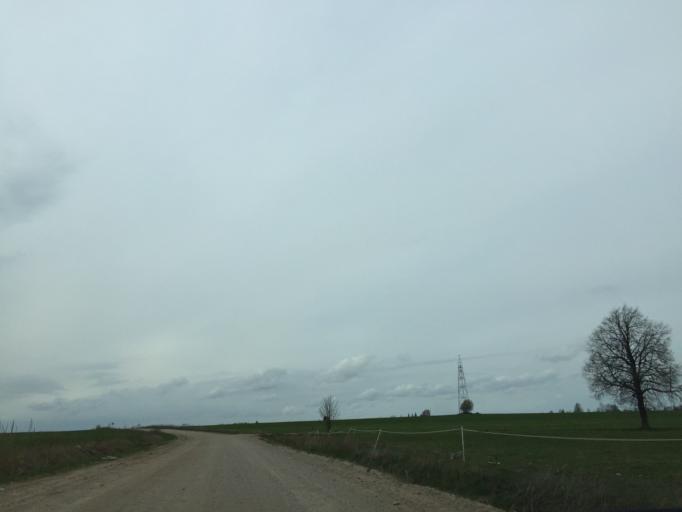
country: LV
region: Priekuli
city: Priekuli
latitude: 57.3412
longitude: 25.3593
